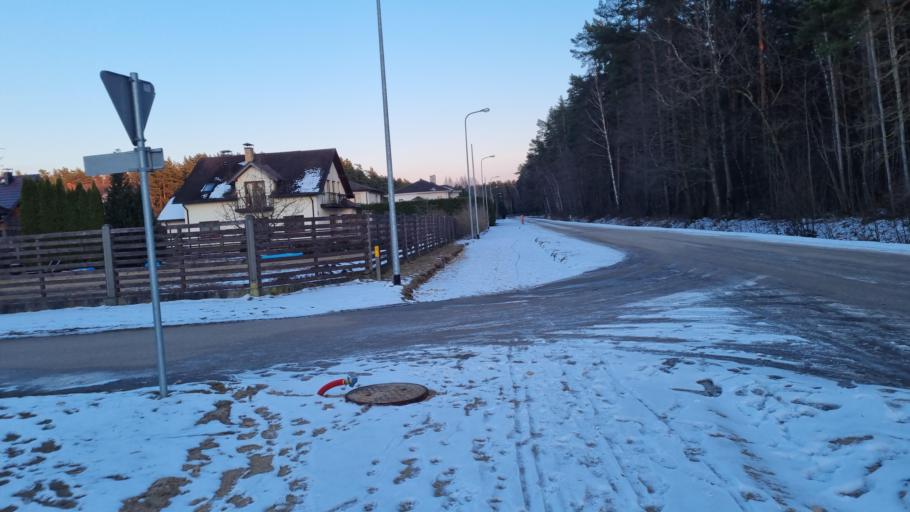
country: LV
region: Babite
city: Pinki
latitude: 56.9668
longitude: 23.9402
